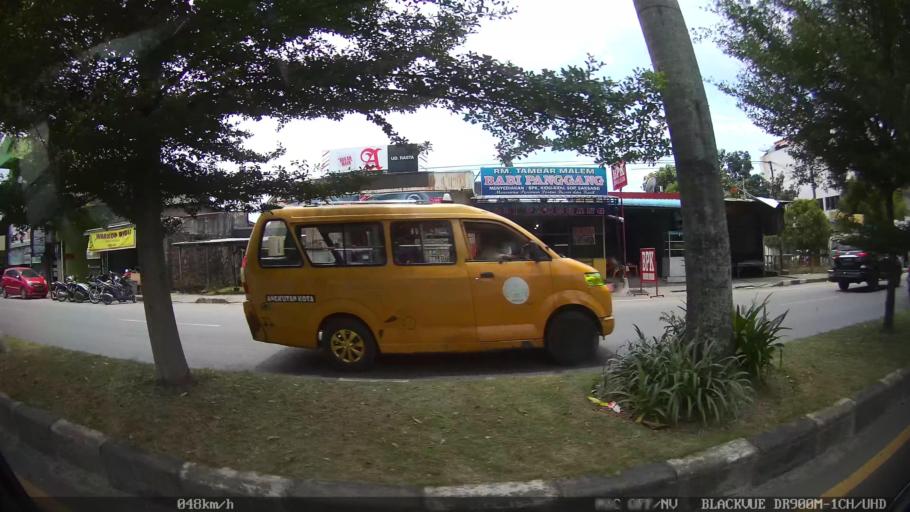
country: ID
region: North Sumatra
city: Deli Tua
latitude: 3.5342
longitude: 98.6492
